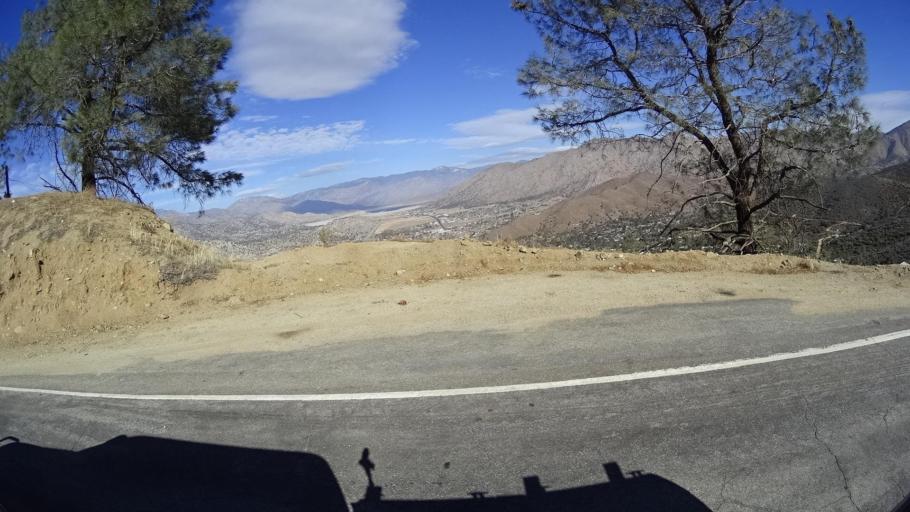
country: US
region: California
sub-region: Kern County
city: Bodfish
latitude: 35.5807
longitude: -118.5047
